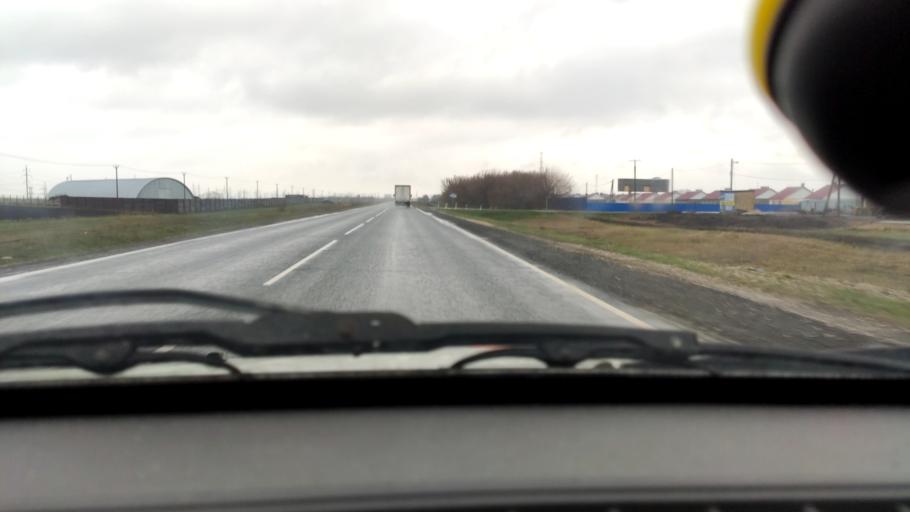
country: RU
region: Samara
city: Povolzhskiy
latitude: 53.6429
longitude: 49.6654
